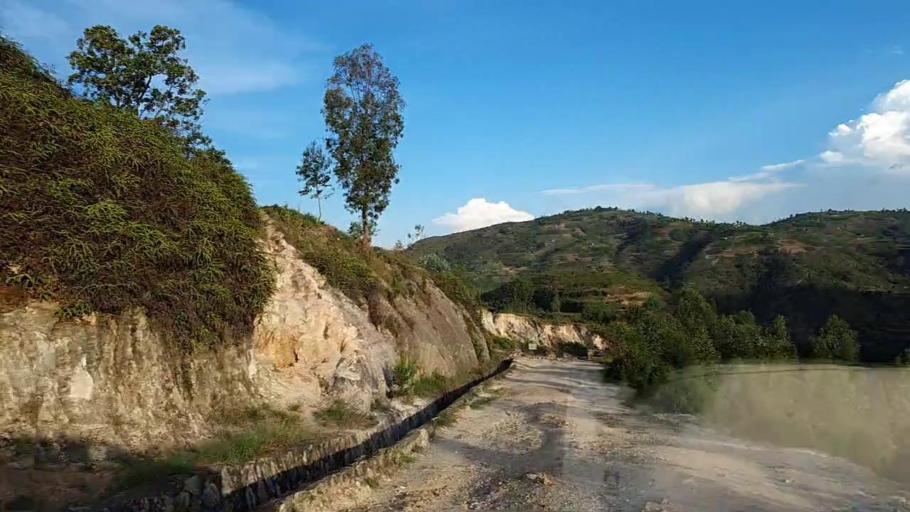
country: RW
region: Southern Province
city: Gikongoro
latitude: -2.3980
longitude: 29.5592
